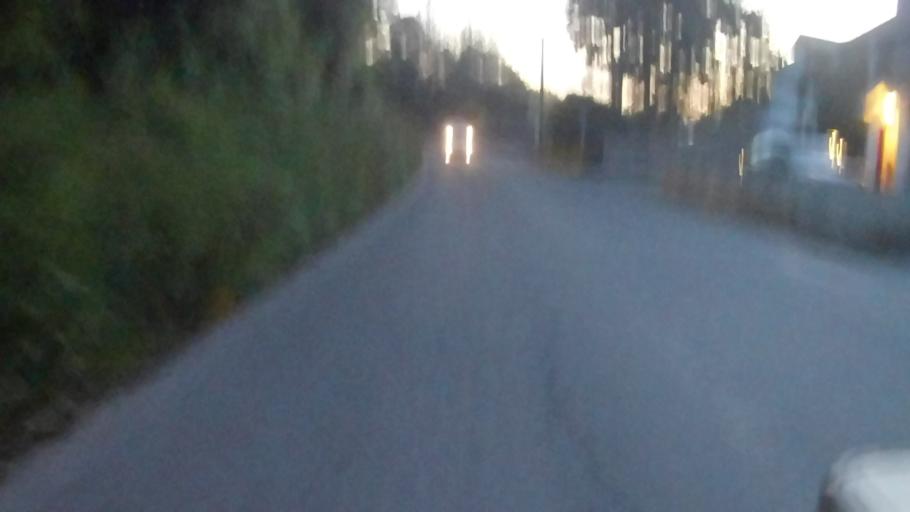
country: IE
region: Munster
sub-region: County Cork
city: Passage West
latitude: 51.9313
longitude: -8.3624
